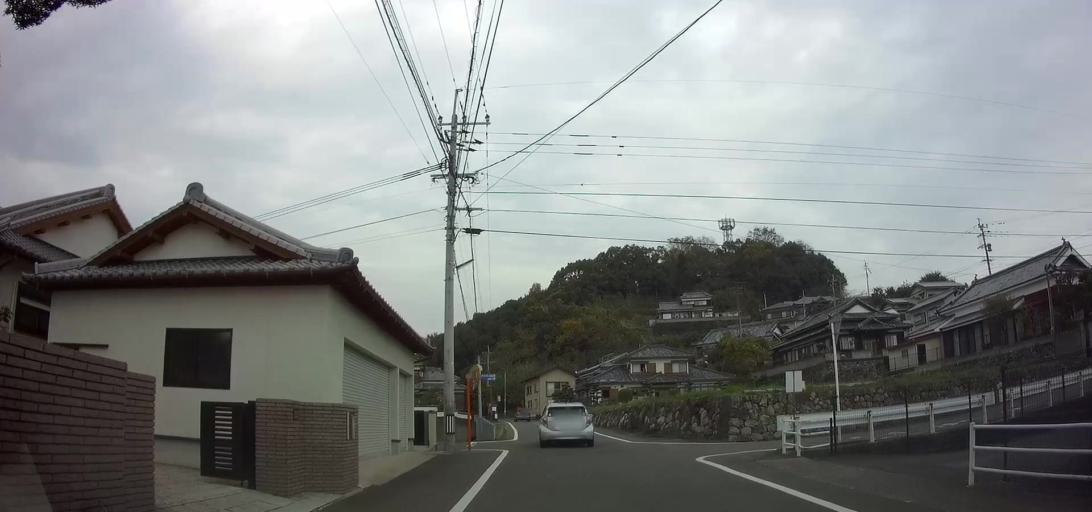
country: JP
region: Kumamoto
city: Hondo
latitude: 32.6345
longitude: 130.2459
